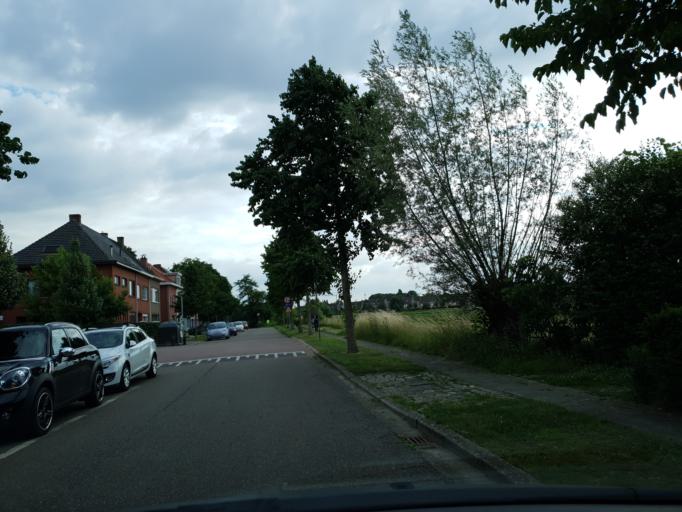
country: BE
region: Flanders
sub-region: Provincie Antwerpen
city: Kapellen
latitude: 51.2745
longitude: 4.4482
